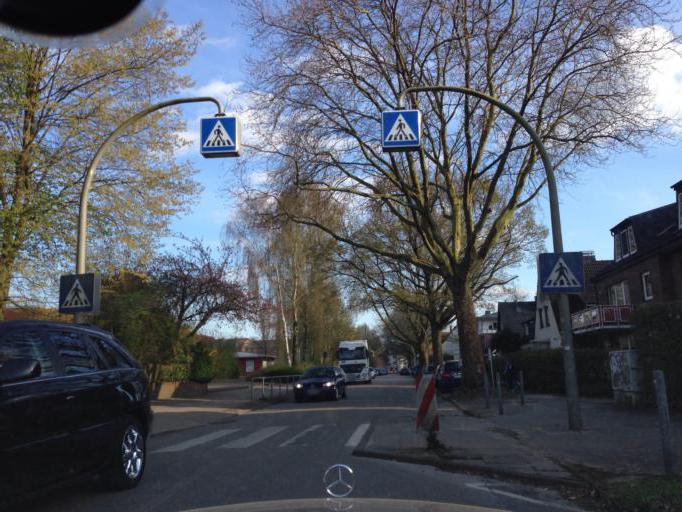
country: DE
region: Hamburg
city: Marienthal
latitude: 53.5836
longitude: 10.0869
